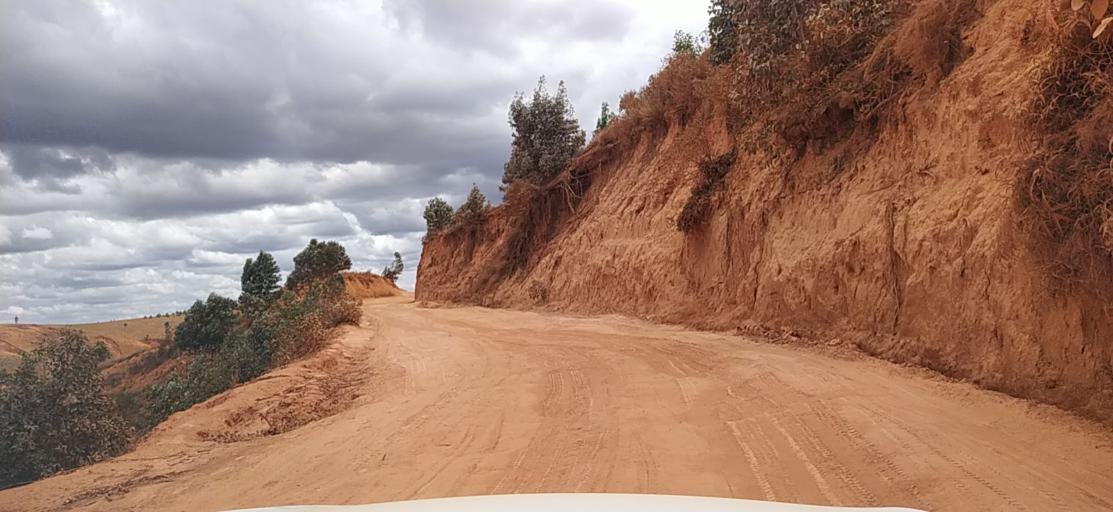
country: MG
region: Alaotra Mangoro
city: Ambatondrazaka
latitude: -18.0496
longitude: 48.2507
